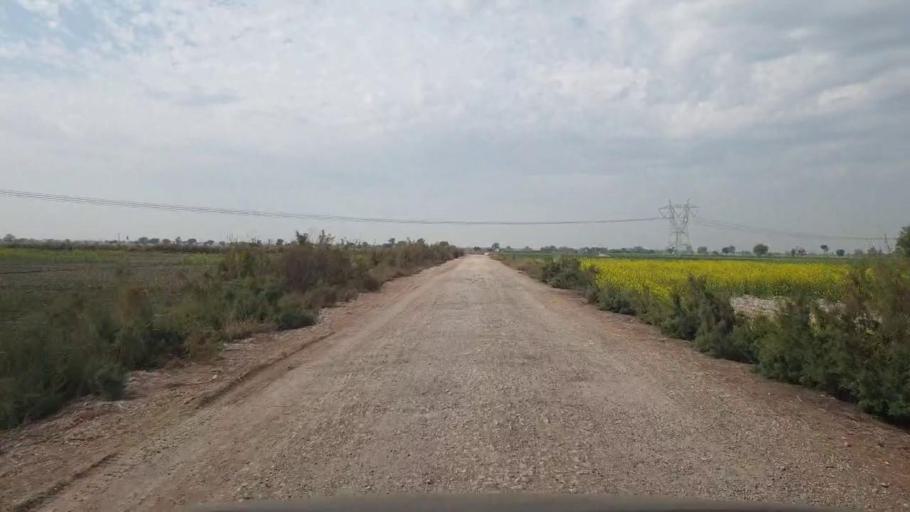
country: PK
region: Sindh
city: Sakrand
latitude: 26.0141
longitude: 68.3874
